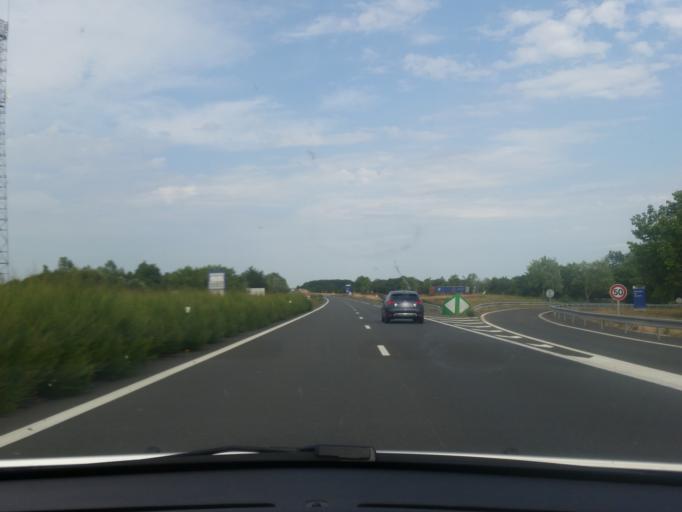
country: FR
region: Pays de la Loire
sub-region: Departement de Maine-et-Loire
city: Saint-Georges-sur-Loire
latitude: 47.4340
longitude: -0.7945
